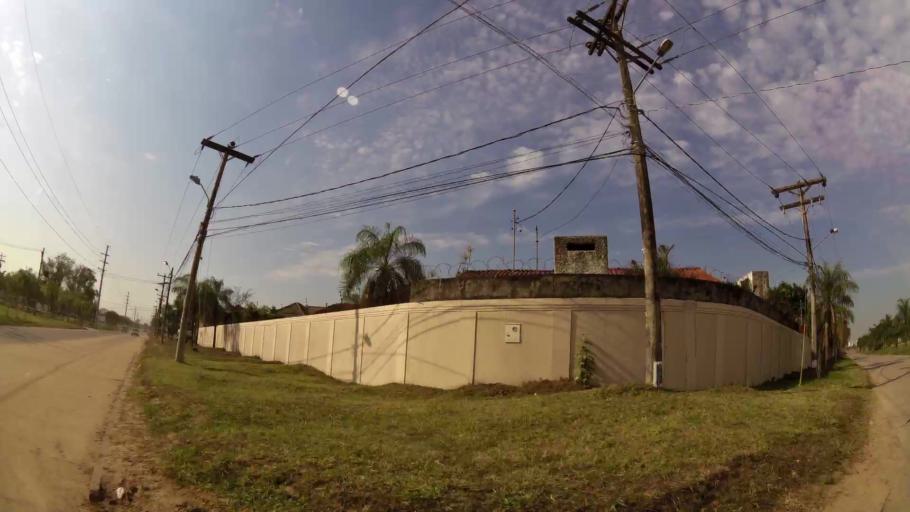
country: BO
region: Santa Cruz
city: Santa Cruz de la Sierra
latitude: -17.7225
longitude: -63.1733
